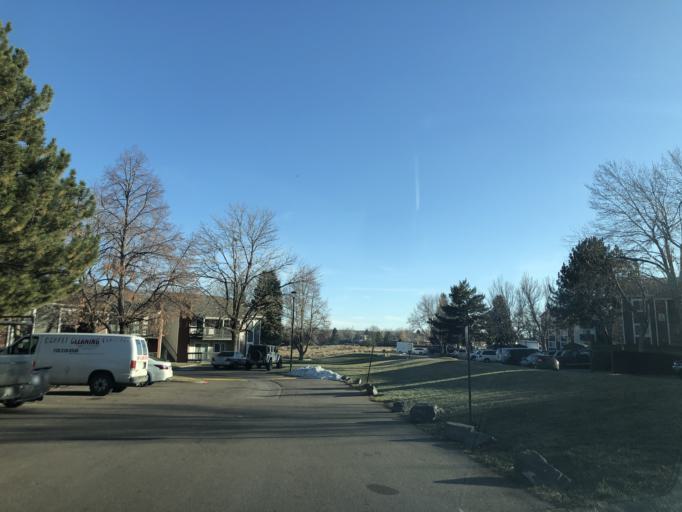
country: US
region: Colorado
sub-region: Adams County
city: Aurora
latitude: 39.7038
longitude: -104.8076
